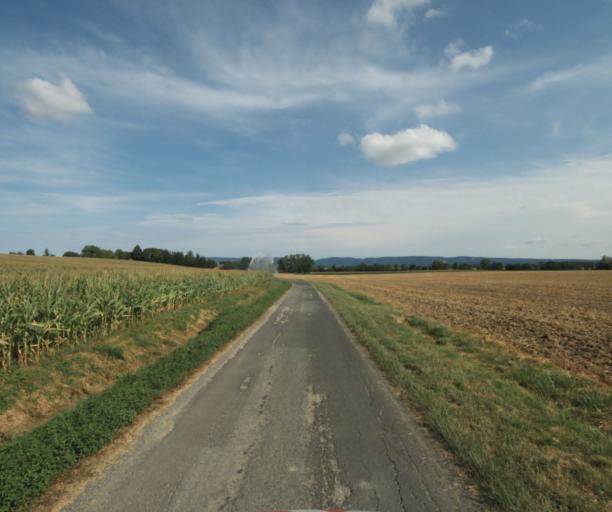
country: FR
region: Midi-Pyrenees
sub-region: Departement du Tarn
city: Puylaurens
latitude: 43.5233
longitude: 1.9788
